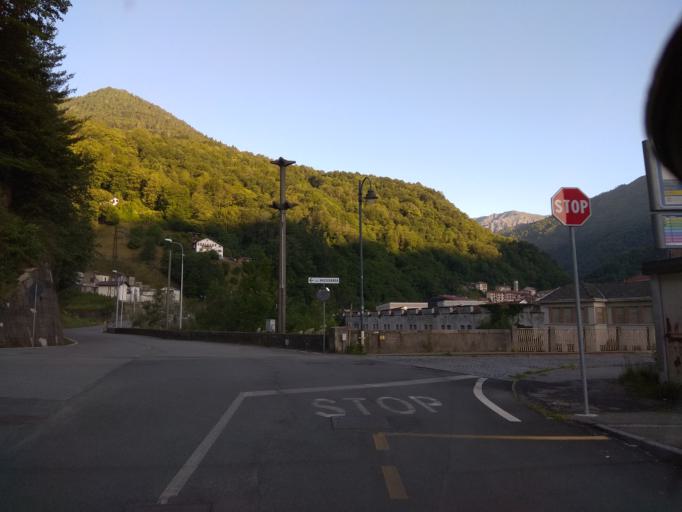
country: IT
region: Piedmont
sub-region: Provincia di Biella
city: Coggiola
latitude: 45.6865
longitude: 8.1761
